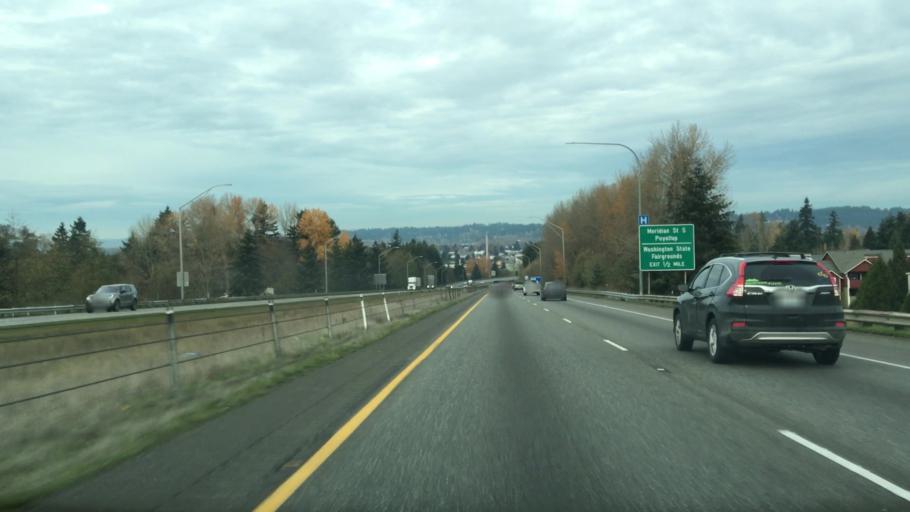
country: US
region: Washington
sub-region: Pierce County
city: Puyallup
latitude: 47.1706
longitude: -122.2967
